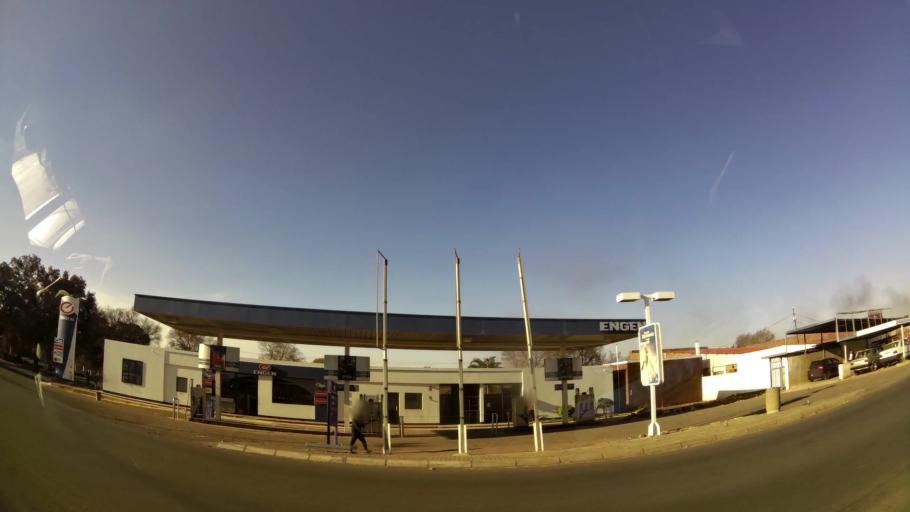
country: ZA
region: Gauteng
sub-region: City of Johannesburg Metropolitan Municipality
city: Roodepoort
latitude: -26.1654
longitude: 27.8705
